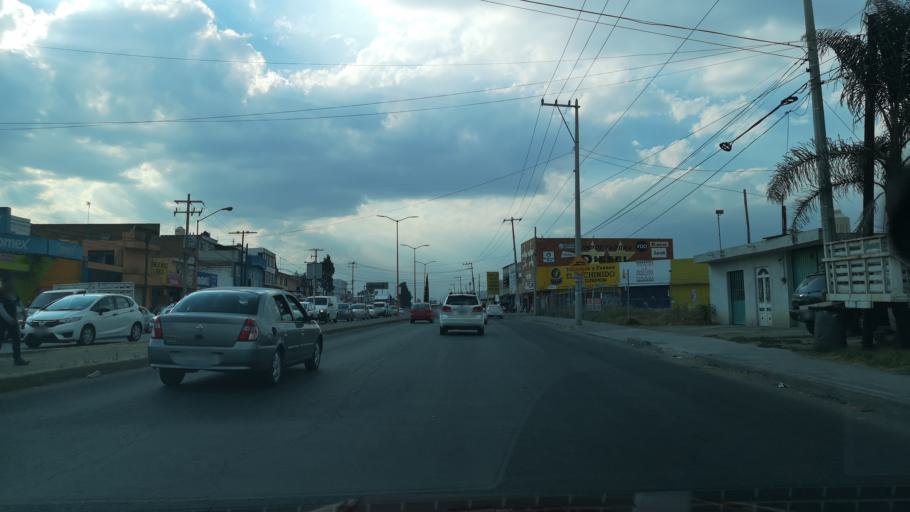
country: MX
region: Puebla
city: Cholula
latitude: 19.0719
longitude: -98.3158
